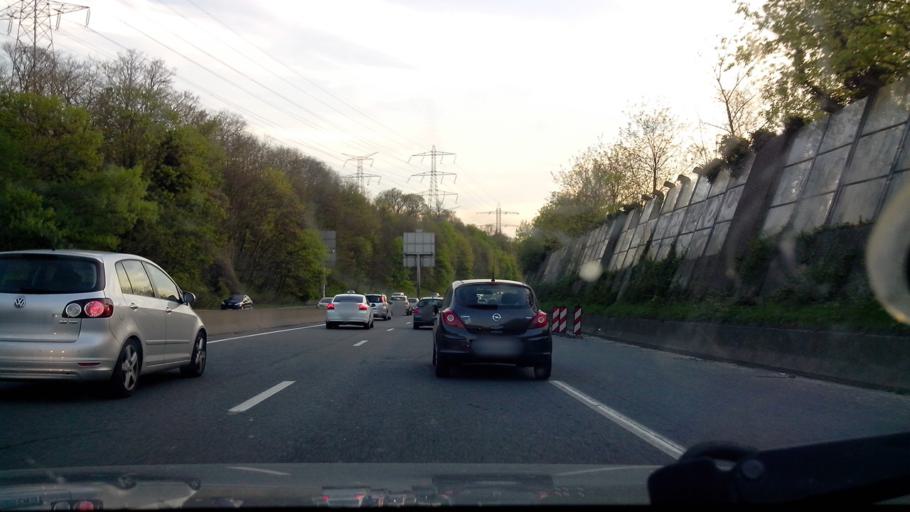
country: FR
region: Ile-de-France
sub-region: Departement de l'Essonne
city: Bievres
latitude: 48.7634
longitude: 2.2288
